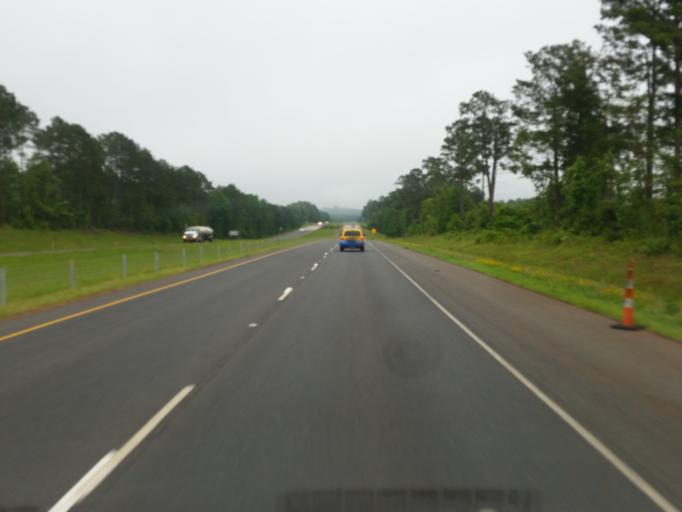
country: US
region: Louisiana
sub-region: Bienville Parish
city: Arcadia
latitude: 32.5633
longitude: -93.0691
